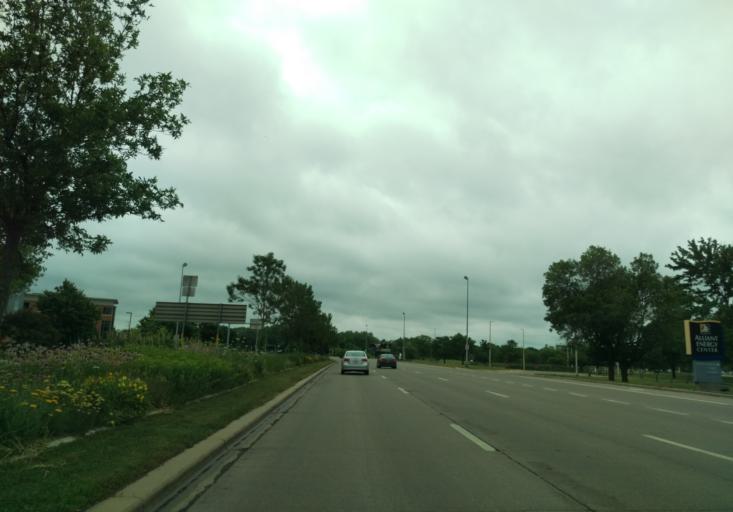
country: US
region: Wisconsin
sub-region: Dane County
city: Madison
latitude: 43.0494
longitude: -89.3771
